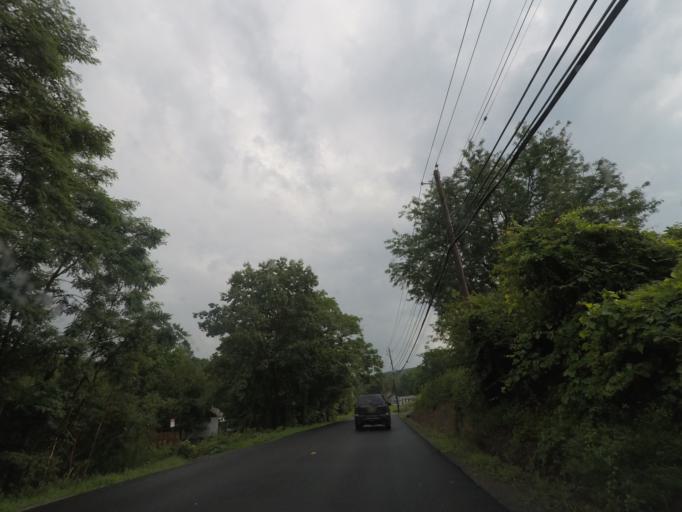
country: US
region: New York
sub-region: Rensselaer County
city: Poestenkill
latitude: 42.6858
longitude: -73.5408
